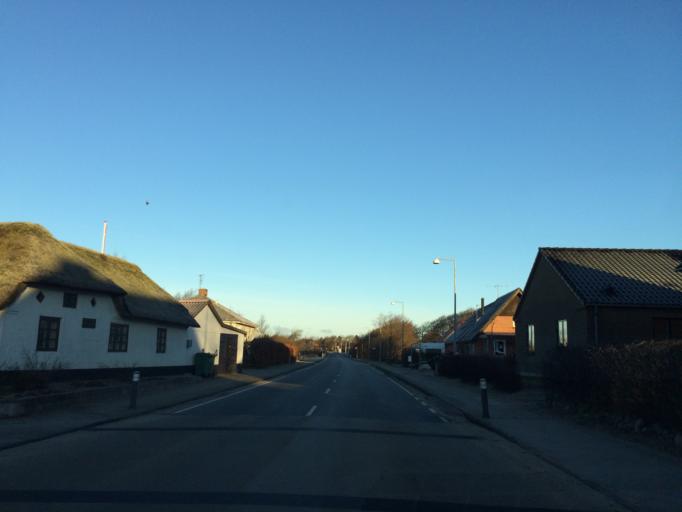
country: DK
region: Central Jutland
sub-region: Lemvig Kommune
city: Lemvig
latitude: 56.4089
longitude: 8.3119
